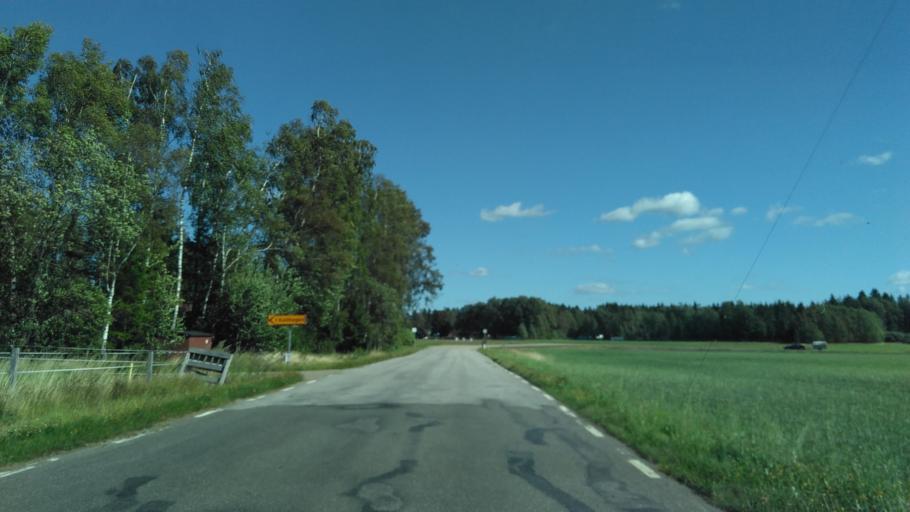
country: SE
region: Vaestra Goetaland
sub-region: Skara Kommun
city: Axvall
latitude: 58.3901
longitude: 13.5256
